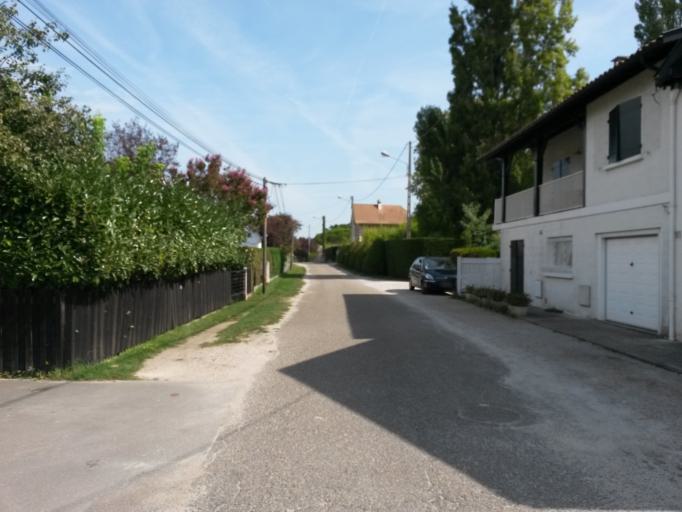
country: FR
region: Aquitaine
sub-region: Departement de la Gironde
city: Lanton
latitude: 44.7001
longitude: -1.0340
